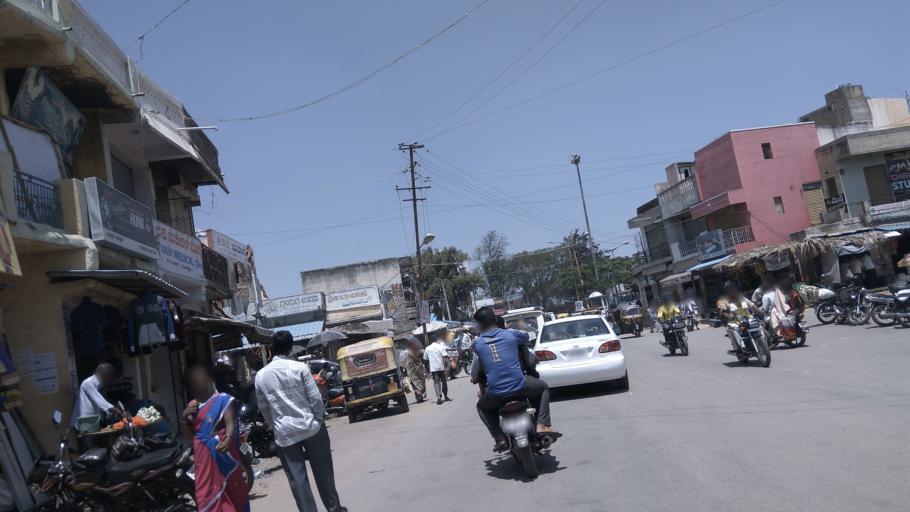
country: IN
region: Karnataka
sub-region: Kolar
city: Mulbagal
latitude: 13.1636
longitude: 78.3938
